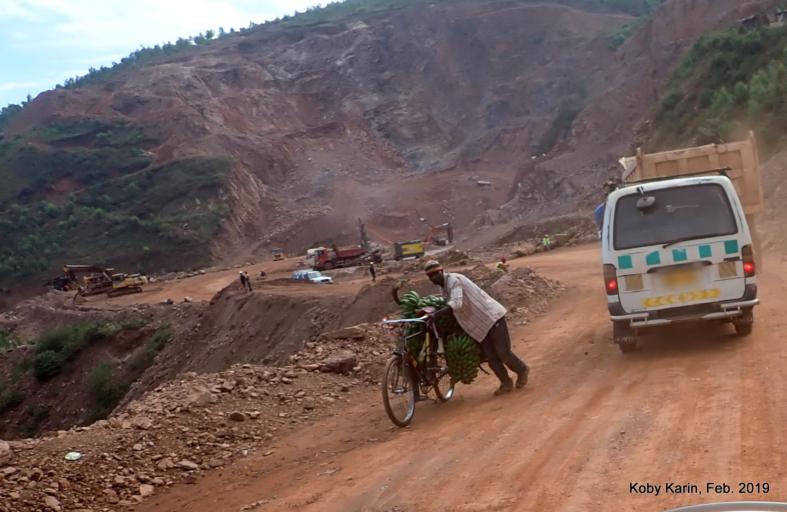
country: RW
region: Eastern Province
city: Kibungo
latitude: -2.1685
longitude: 30.5738
